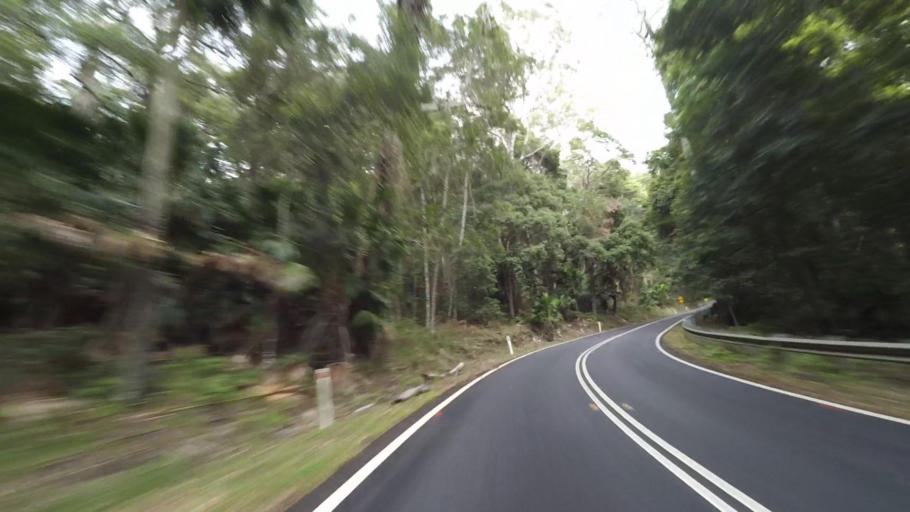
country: AU
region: New South Wales
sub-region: Wollongong
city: Helensburgh
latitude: -34.1571
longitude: 151.0212
